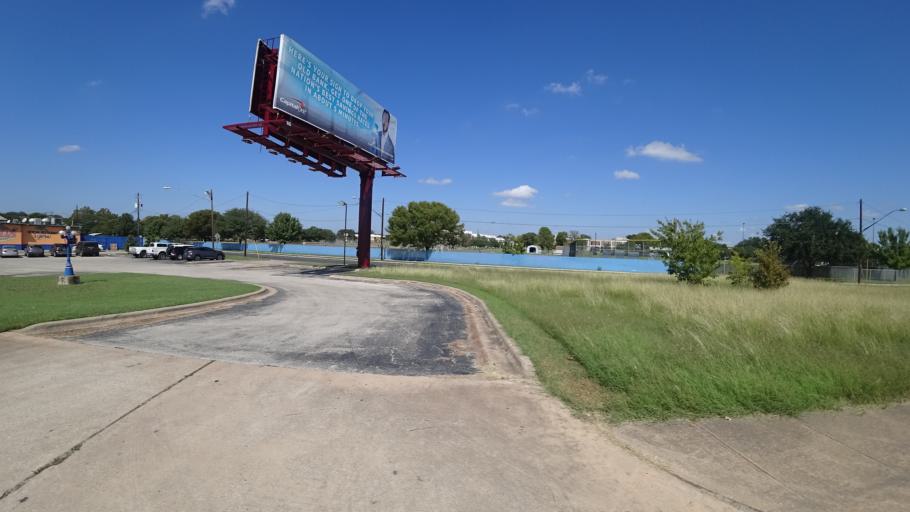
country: US
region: Texas
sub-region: Travis County
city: Austin
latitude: 30.3217
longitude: -97.6923
